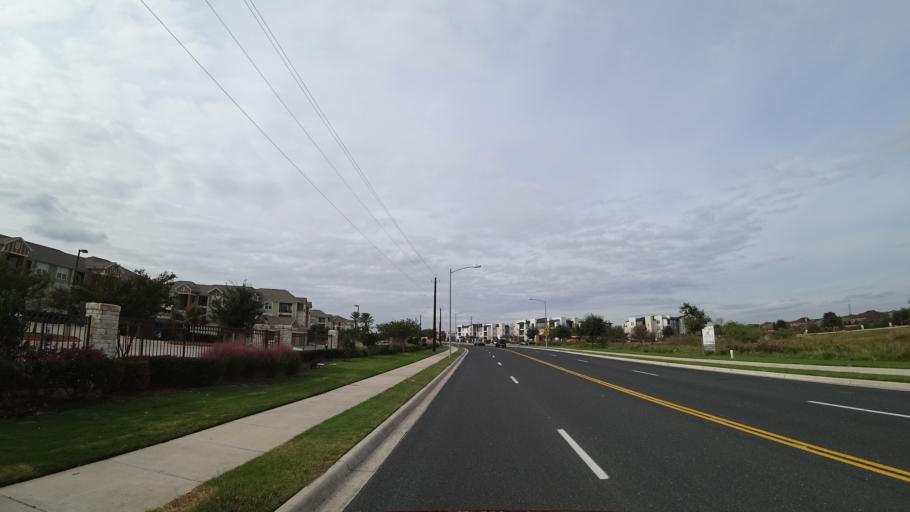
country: US
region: Texas
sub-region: Travis County
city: Wells Branch
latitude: 30.4279
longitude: -97.6648
